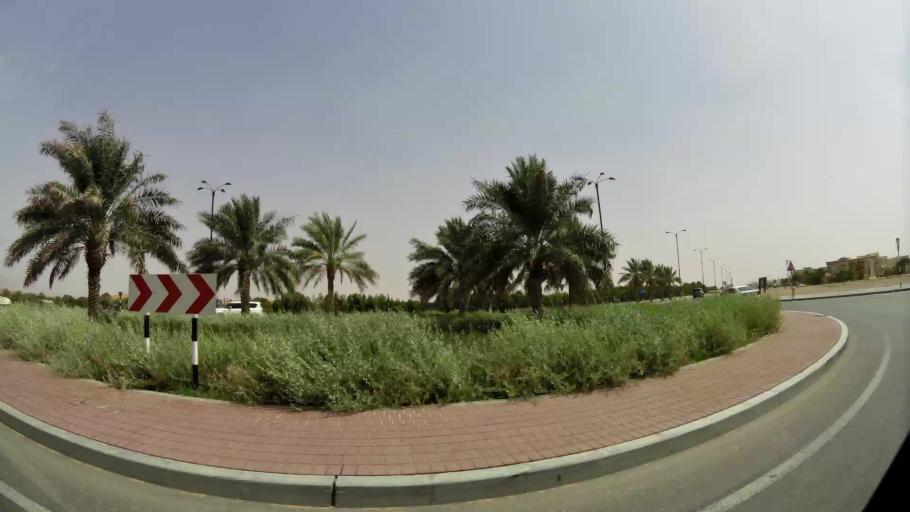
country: AE
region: Abu Dhabi
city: Al Ain
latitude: 24.1511
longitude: 55.6569
